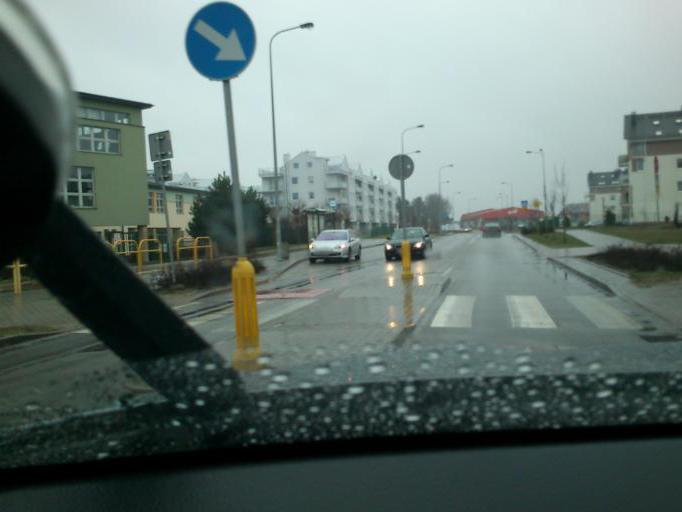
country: PL
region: Pomeranian Voivodeship
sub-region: Gdynia
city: Wielki Kack
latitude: 54.4213
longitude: 18.4786
